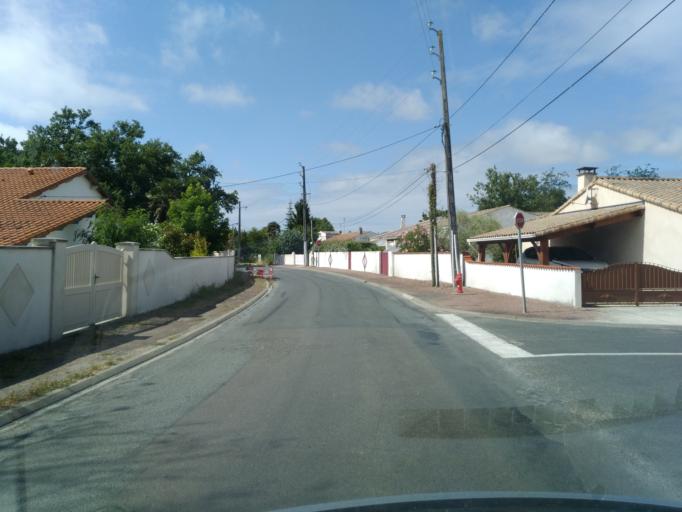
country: FR
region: Poitou-Charentes
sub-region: Departement de la Charente-Maritime
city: Breuillet
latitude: 45.6964
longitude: -1.0664
